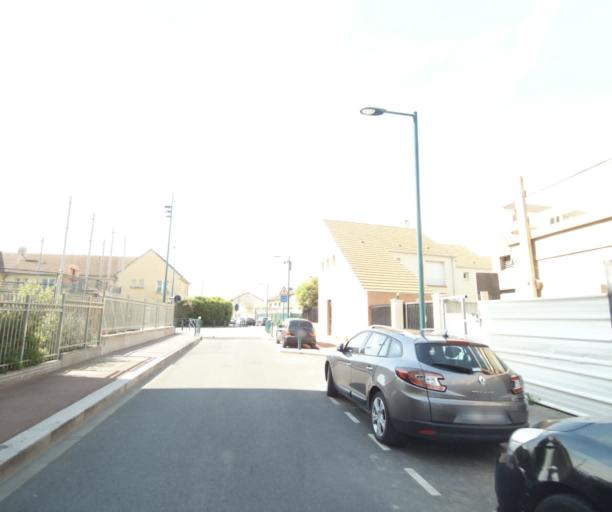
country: FR
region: Ile-de-France
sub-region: Departement des Hauts-de-Seine
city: Gennevilliers
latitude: 48.9322
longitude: 2.2916
